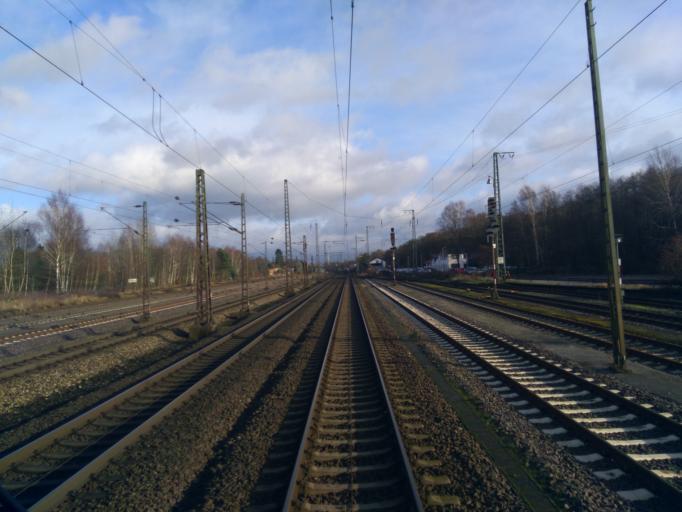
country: DE
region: Lower Saxony
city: Rotenburg
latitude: 53.1113
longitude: 9.3825
